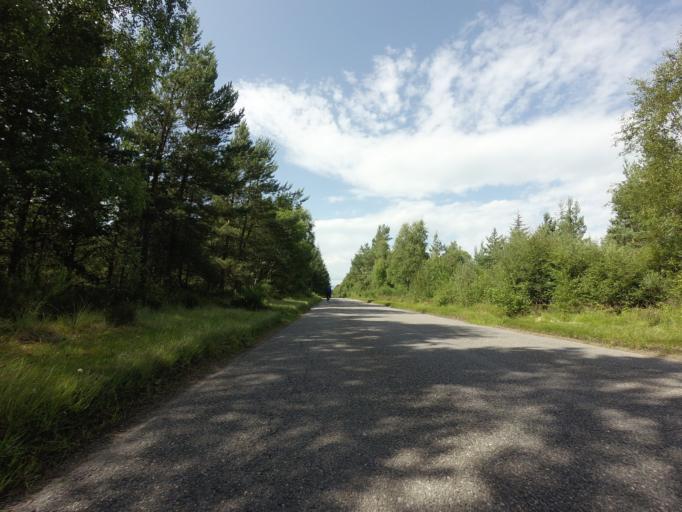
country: GB
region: Scotland
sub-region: Highland
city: Fortrose
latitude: 57.4814
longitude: -4.0898
